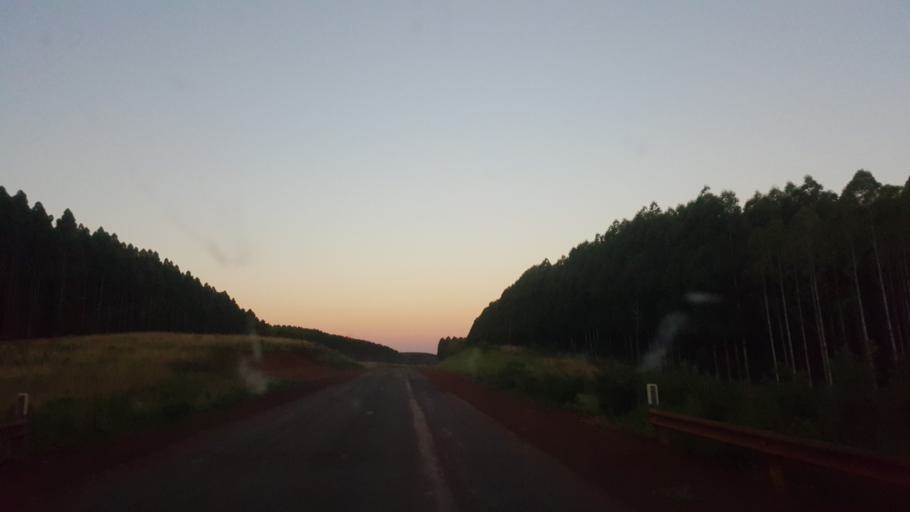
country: AR
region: Corrientes
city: Garruchos
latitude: -28.2515
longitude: -55.8480
